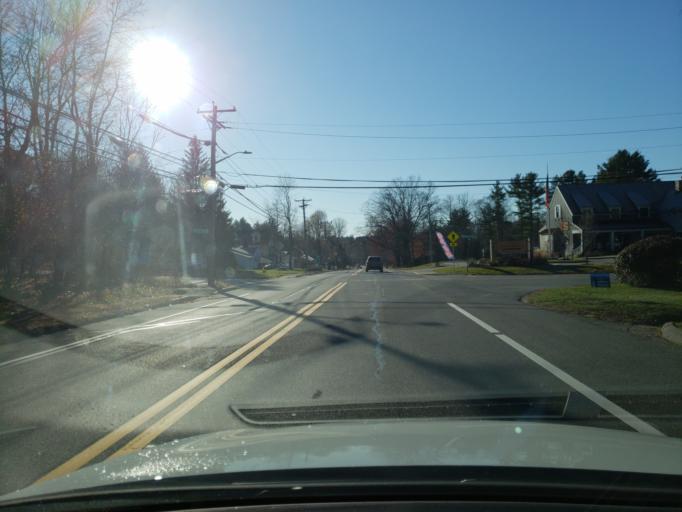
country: US
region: Massachusetts
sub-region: Essex County
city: Andover
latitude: 42.6193
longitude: -71.1253
